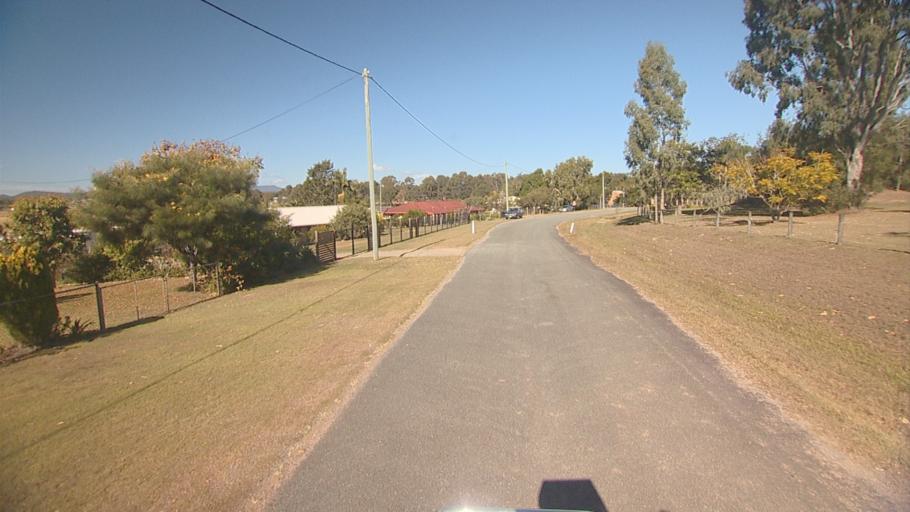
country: AU
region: Queensland
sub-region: Logan
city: Chambers Flat
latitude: -27.7609
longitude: 153.0945
